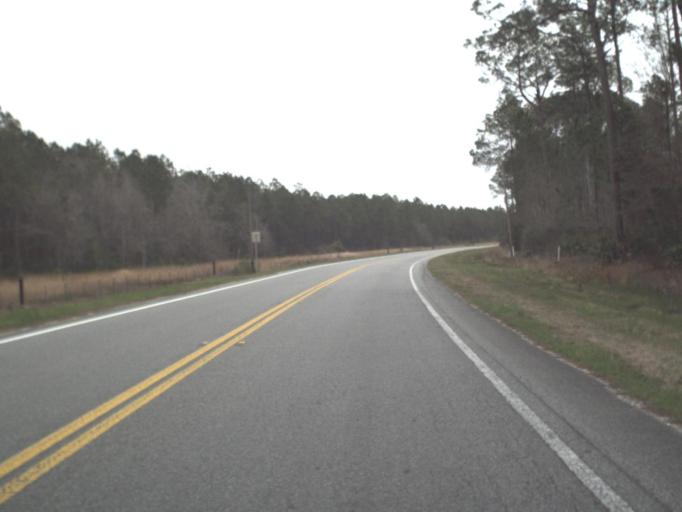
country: US
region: Florida
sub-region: Leon County
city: Woodville
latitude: 30.1994
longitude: -84.1702
